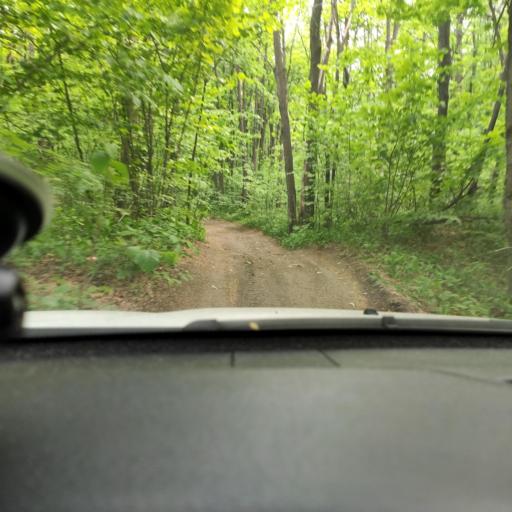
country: RU
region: Samara
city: Samara
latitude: 53.3194
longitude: 50.2010
